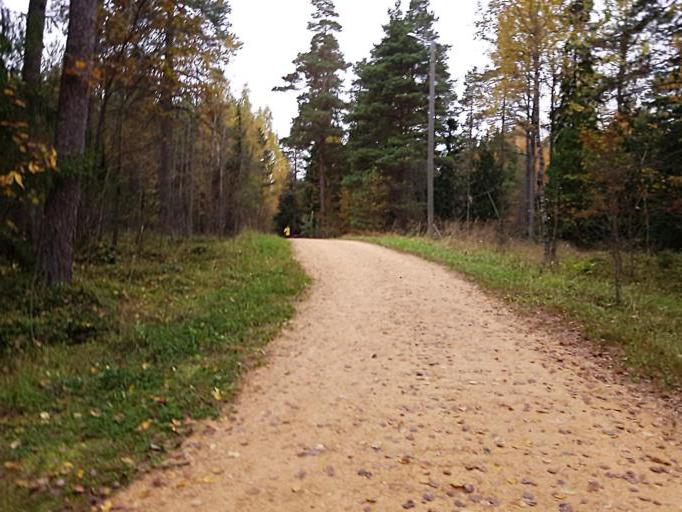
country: FI
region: Uusimaa
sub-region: Helsinki
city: Helsinki
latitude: 60.2644
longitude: 24.9128
